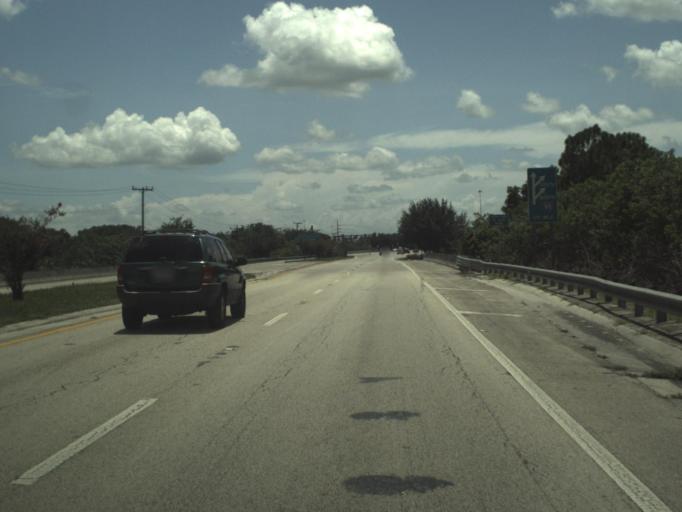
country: US
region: Florida
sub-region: Martin County
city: Palm City
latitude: 27.1145
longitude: -80.2554
